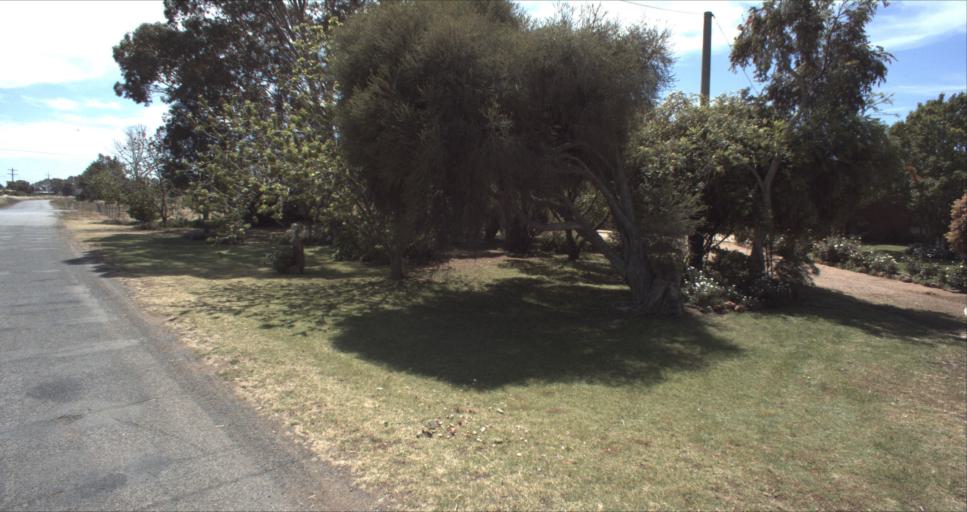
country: AU
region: New South Wales
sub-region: Leeton
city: Leeton
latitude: -34.5866
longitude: 146.4275
